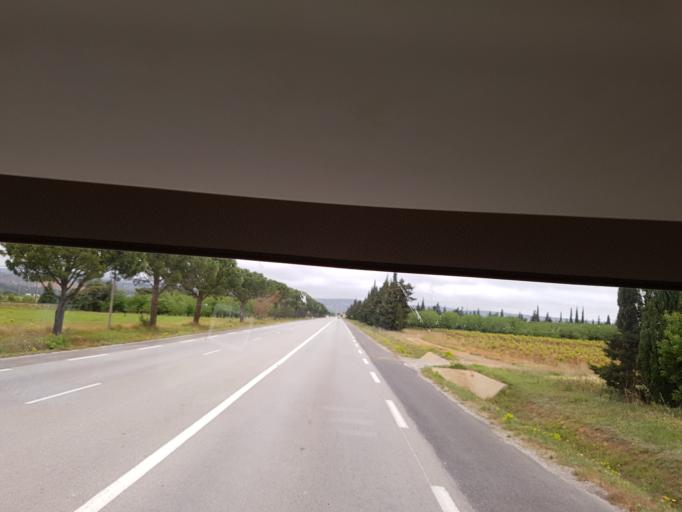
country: FR
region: Languedoc-Roussillon
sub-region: Departement des Pyrenees-Orientales
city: Salses-le-Chateau
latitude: 42.8156
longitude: 2.9146
